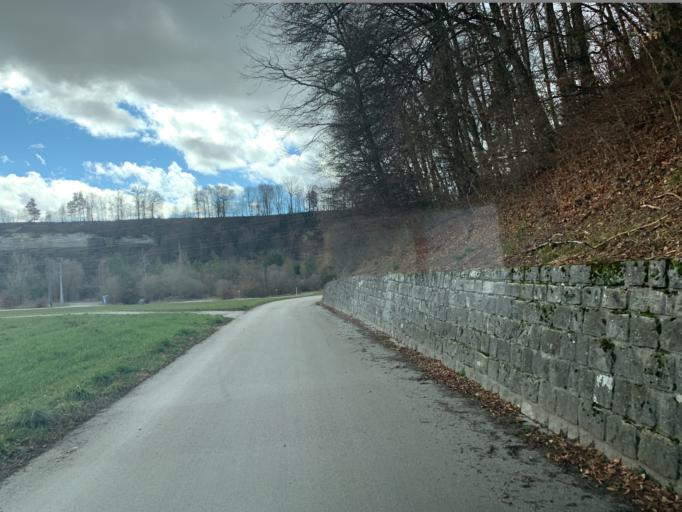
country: CH
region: Fribourg
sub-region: Sense District
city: Bosingen
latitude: 46.8826
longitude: 7.1975
